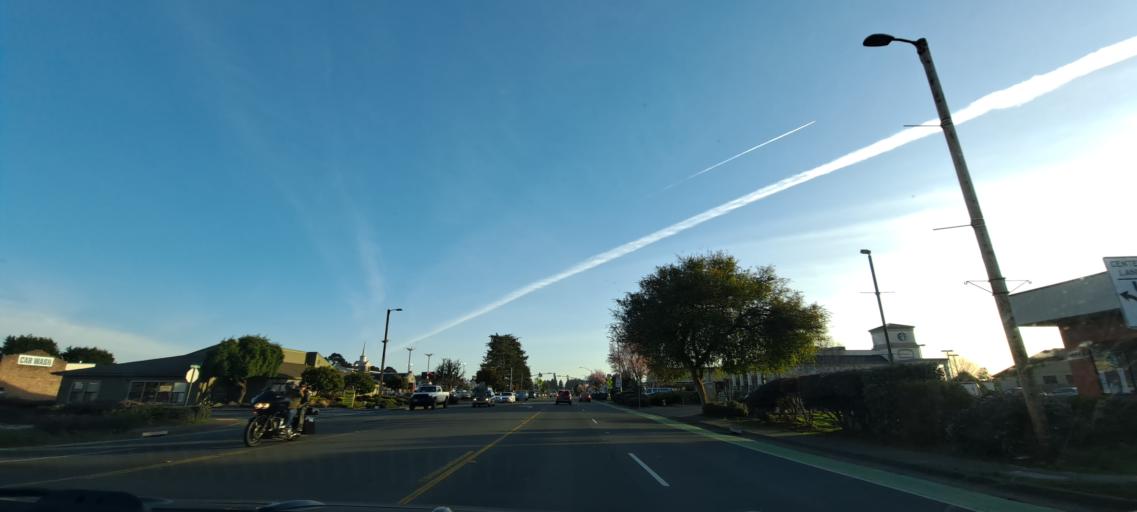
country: US
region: California
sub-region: Humboldt County
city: McKinleyville
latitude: 40.9410
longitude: -124.1010
